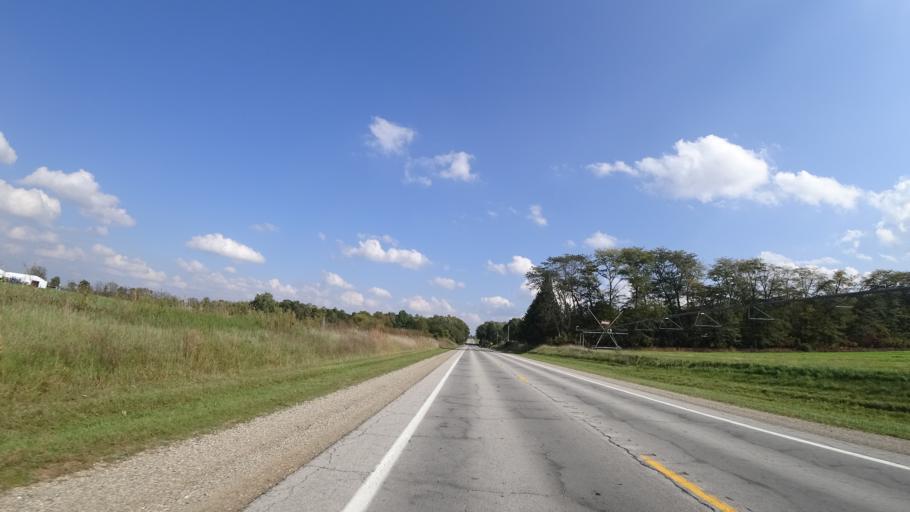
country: US
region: Michigan
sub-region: Saint Joseph County
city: Colon
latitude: 42.0103
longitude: -85.3918
